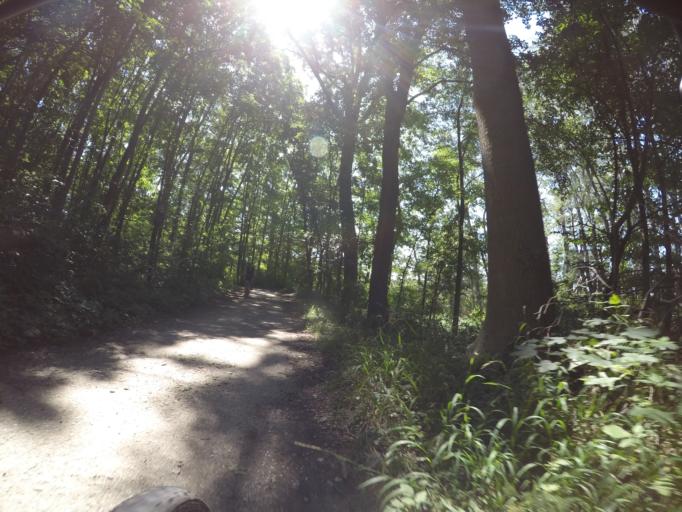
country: AT
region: Lower Austria
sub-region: Politischer Bezirk Wien-Umgebung
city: Schwechat
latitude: 48.1911
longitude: 16.4873
